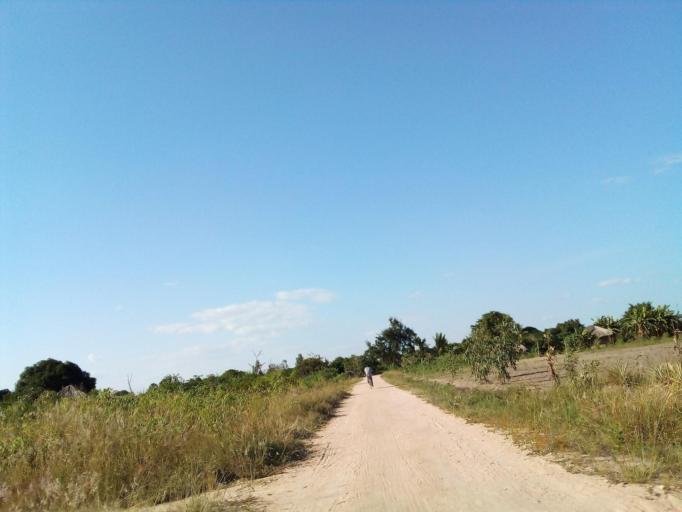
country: MZ
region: Zambezia
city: Quelimane
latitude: -17.5226
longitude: 36.6833
